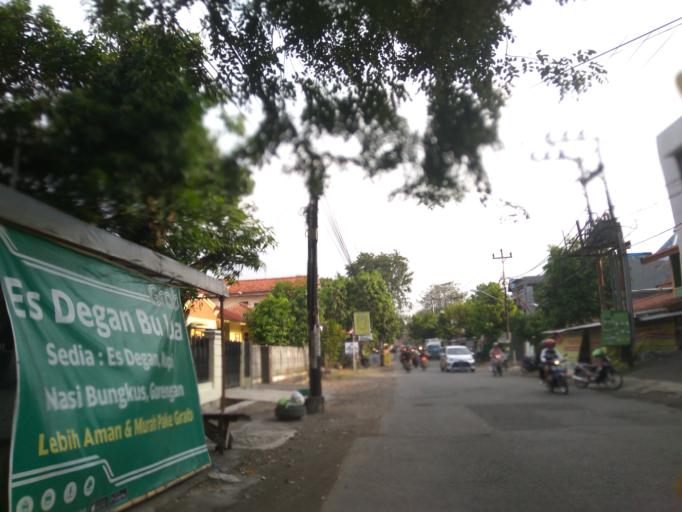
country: ID
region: Central Java
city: Semarang
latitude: -7.0107
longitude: 110.3961
